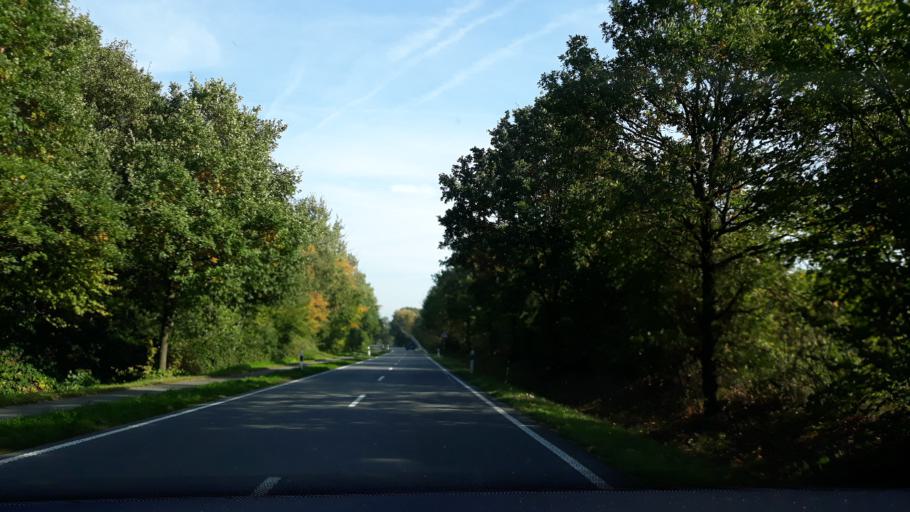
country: DE
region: Schleswig-Holstein
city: Dannewerk
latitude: 54.4788
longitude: 9.5230
